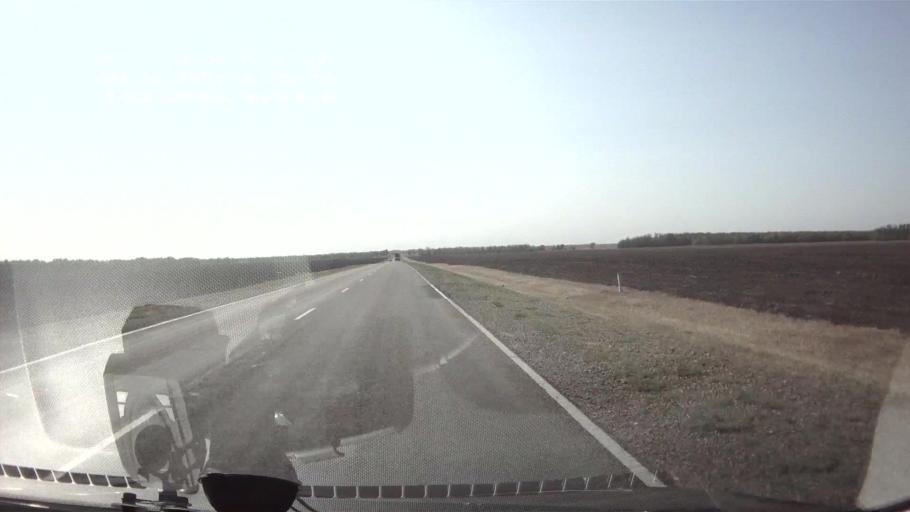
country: RU
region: Krasnodarskiy
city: Belaya Glina
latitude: 46.0292
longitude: 40.7981
